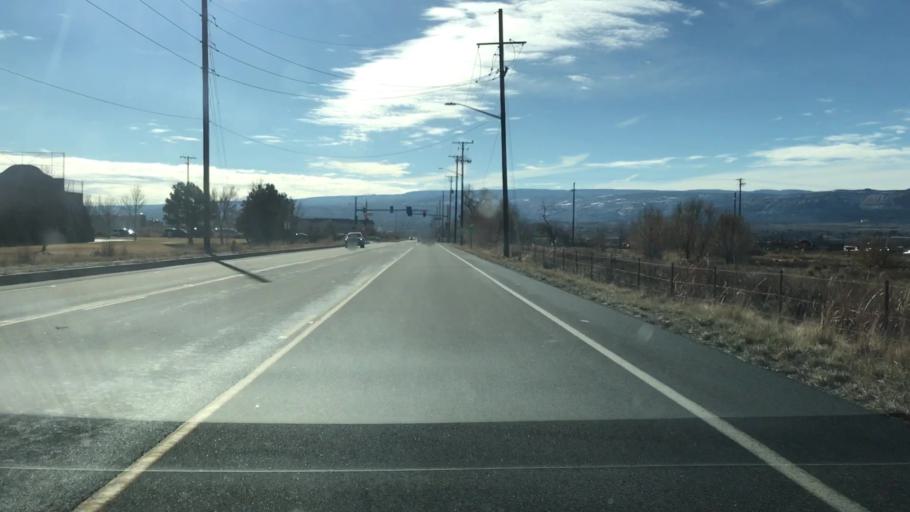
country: US
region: Colorado
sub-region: Mesa County
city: Redlands
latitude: 39.1079
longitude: -108.6082
